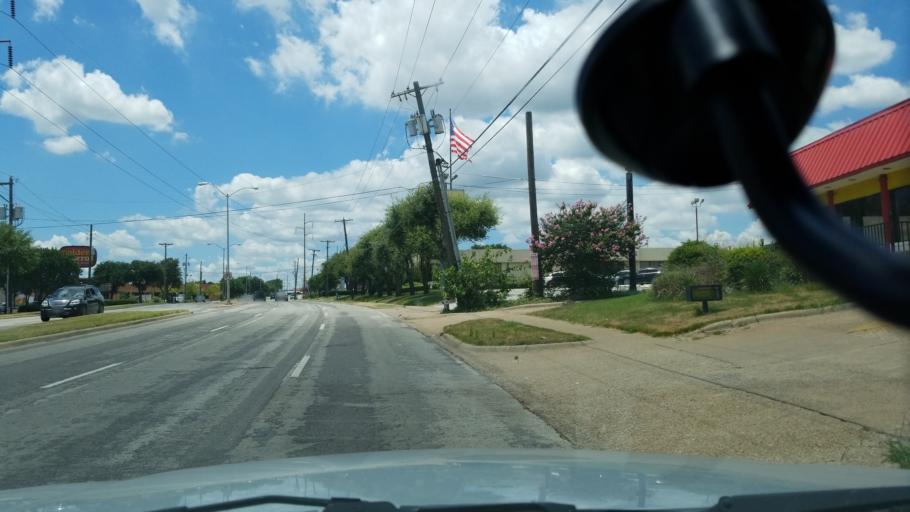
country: US
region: Texas
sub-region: Dallas County
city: Duncanville
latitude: 32.6627
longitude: -96.8767
